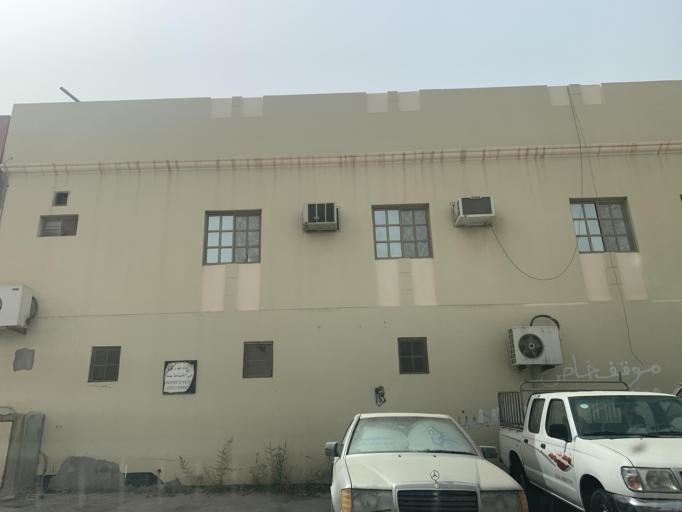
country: BH
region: Northern
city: Madinat `Isa
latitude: 26.1595
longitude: 50.5715
